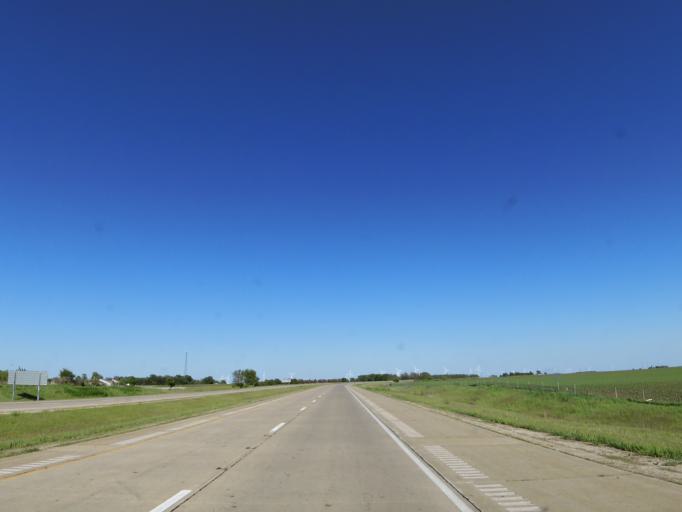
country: US
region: Illinois
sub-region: Woodford County
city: Minonk
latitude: 40.8926
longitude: -89.0473
